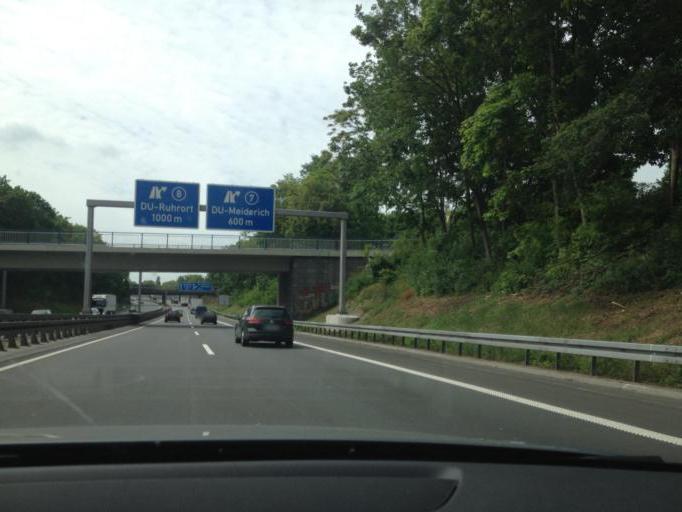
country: DE
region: North Rhine-Westphalia
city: Meiderich
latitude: 51.4766
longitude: 6.7678
